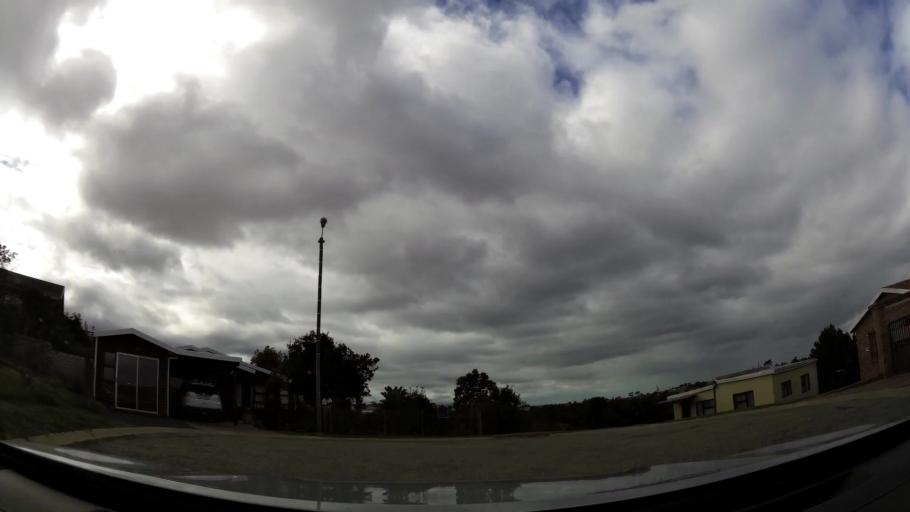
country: ZA
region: Western Cape
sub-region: Eden District Municipality
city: George
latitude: -34.0218
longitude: 22.4784
